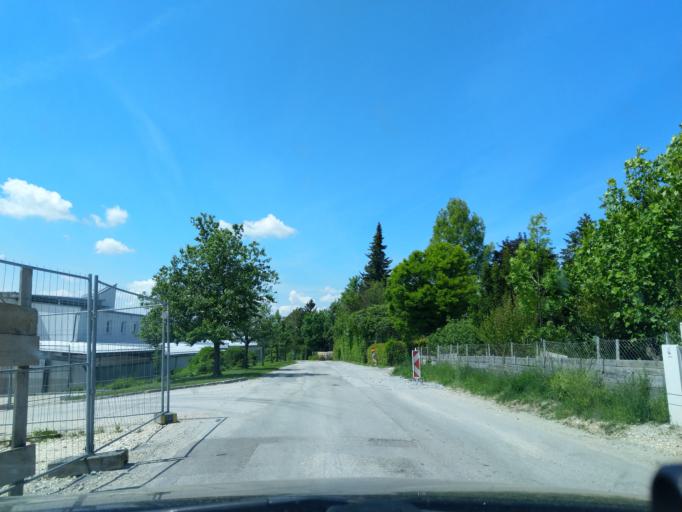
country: AT
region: Upper Austria
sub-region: Politischer Bezirk Ried im Innkreis
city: Ried im Innkreis
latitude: 48.2096
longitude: 13.5278
